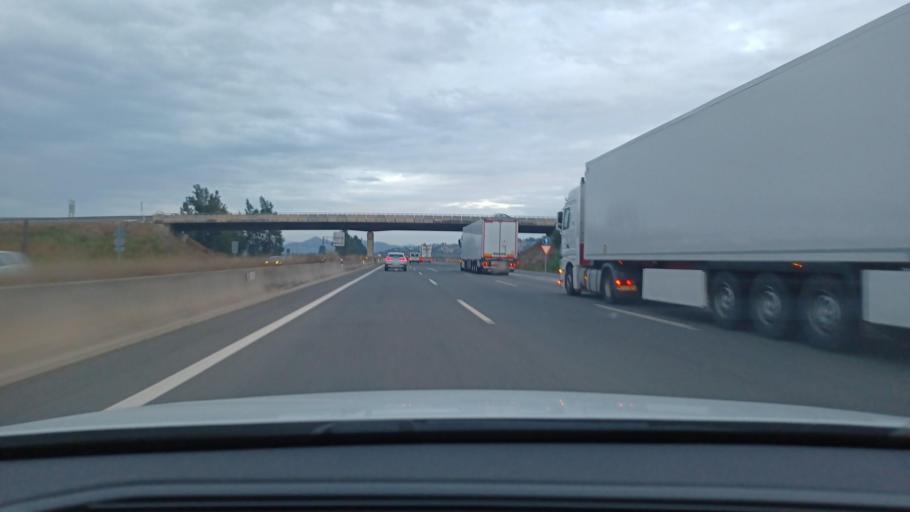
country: ES
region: Valencia
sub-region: Provincia de Valencia
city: Alberic
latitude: 39.1194
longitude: -0.5316
